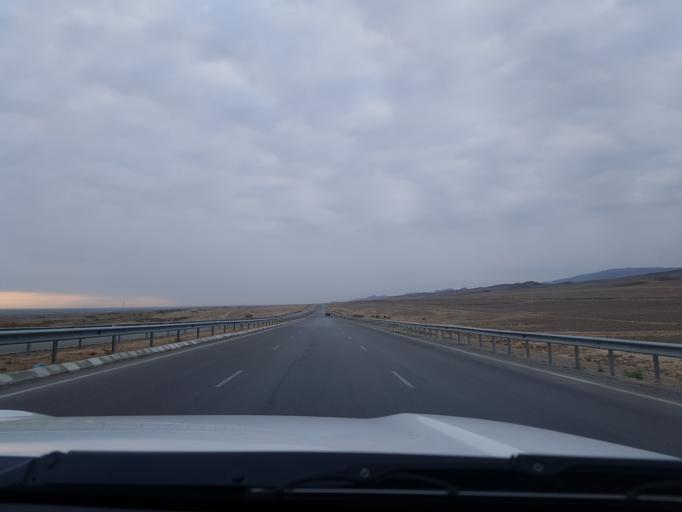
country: IR
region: Razavi Khorasan
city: Dargaz
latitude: 37.6808
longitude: 59.0853
